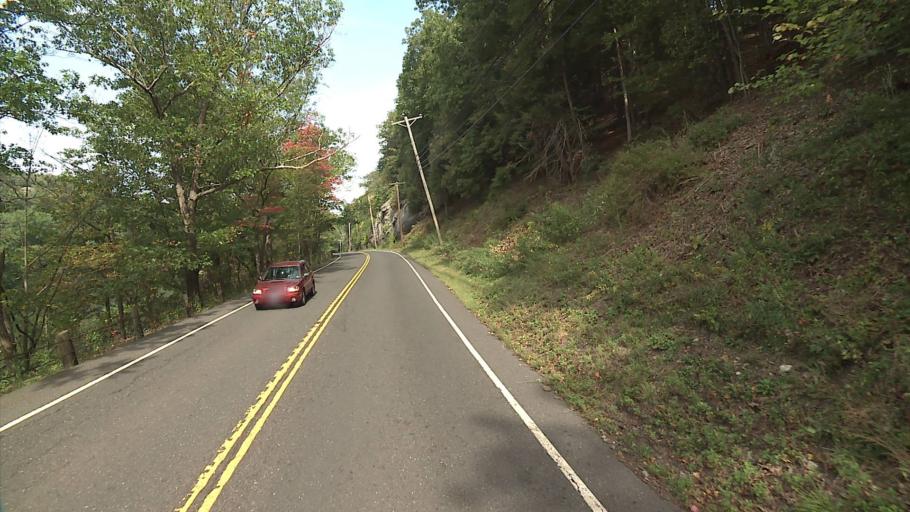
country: US
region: Connecticut
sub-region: New Haven County
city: Oxford
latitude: 41.3755
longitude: -73.1544
